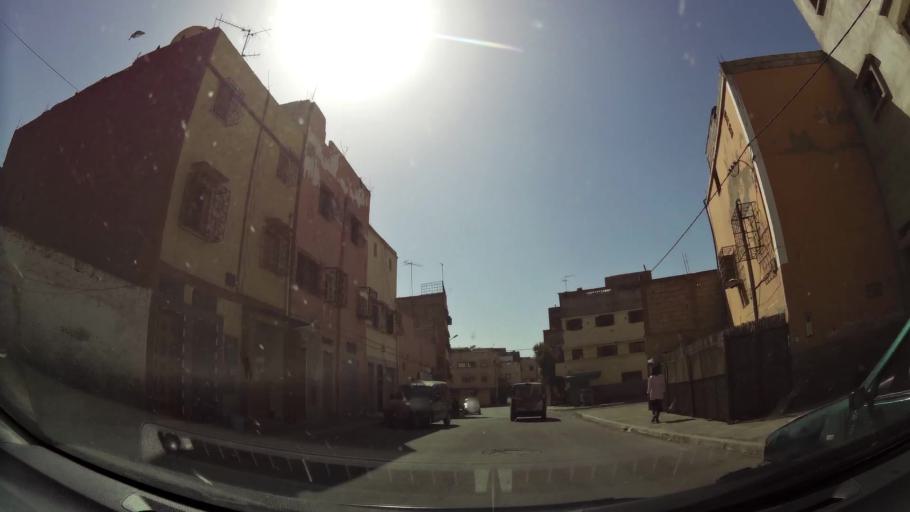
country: MA
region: Souss-Massa-Draa
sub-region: Inezgane-Ait Mellou
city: Inezgane
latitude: 30.3561
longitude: -9.5485
